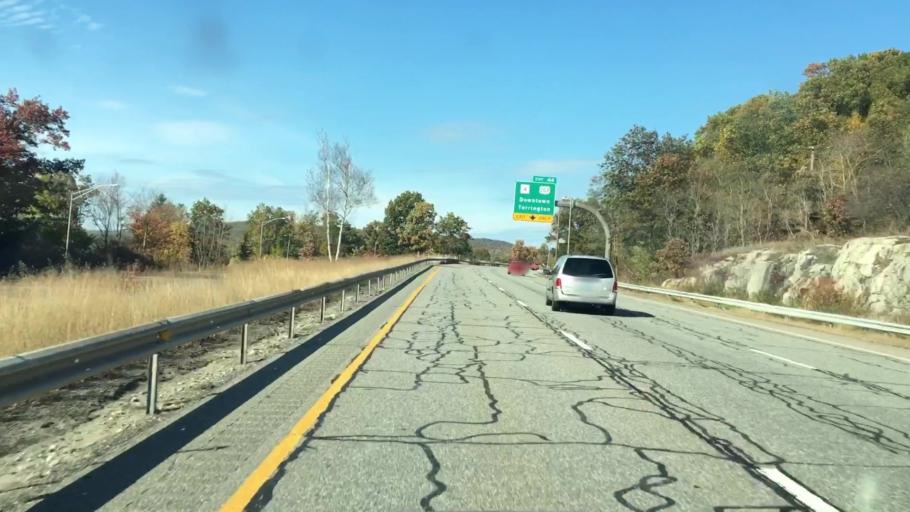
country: US
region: Connecticut
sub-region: Litchfield County
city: Torrington
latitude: 41.7971
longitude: -73.1120
